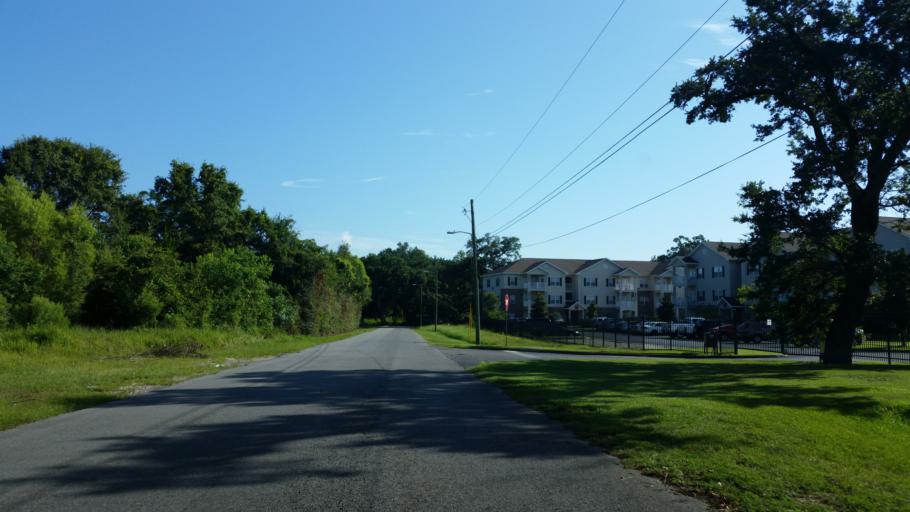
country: US
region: Florida
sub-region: Escambia County
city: Ferry Pass
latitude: 30.5071
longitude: -87.2246
